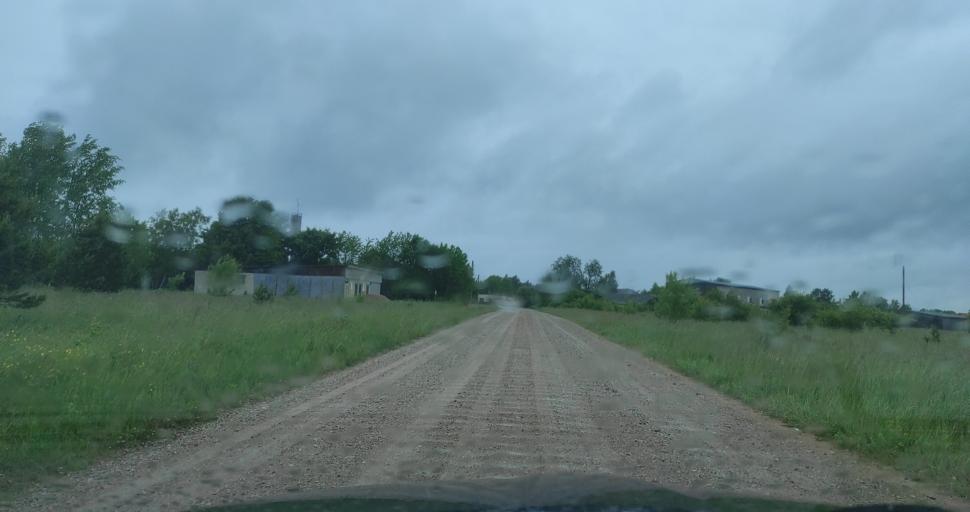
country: LV
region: Alsunga
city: Alsunga
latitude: 57.0025
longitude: 21.3898
